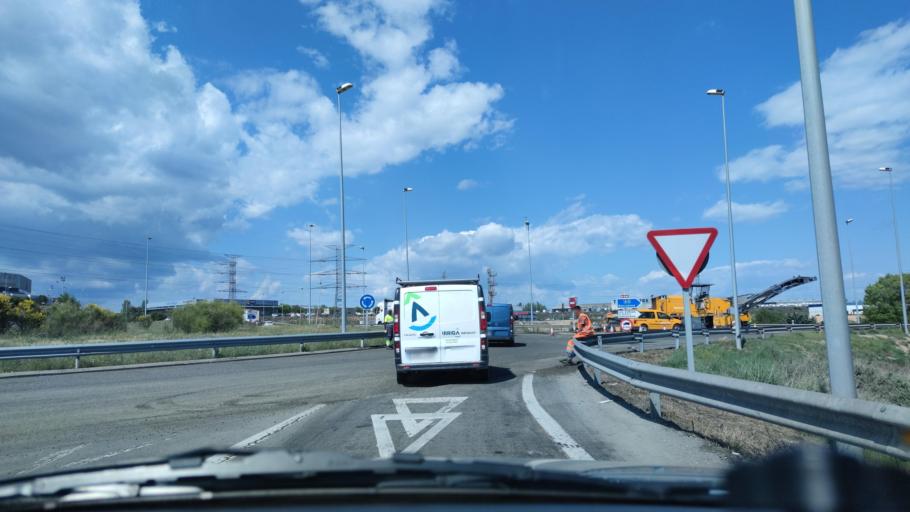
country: ES
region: Catalonia
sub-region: Provincia de Lleida
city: Alcoletge
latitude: 41.6060
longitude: 0.6731
